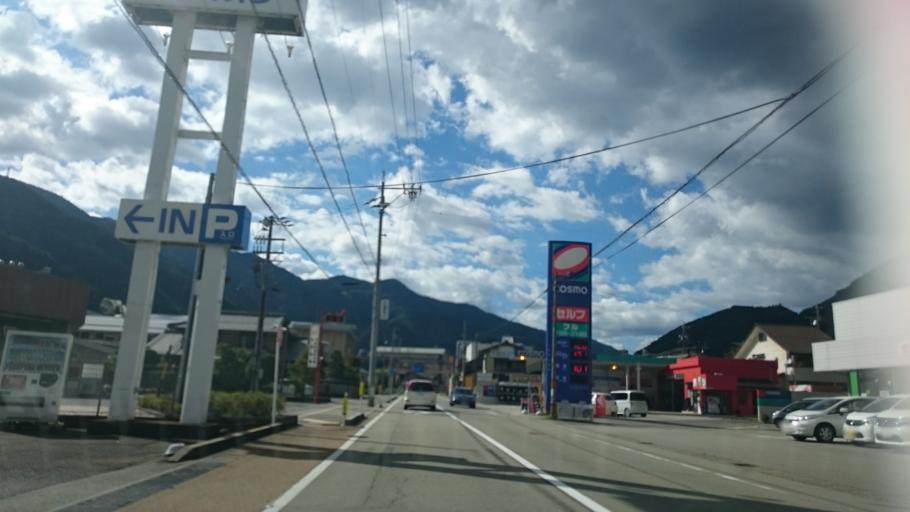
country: JP
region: Gifu
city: Gujo
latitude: 35.8007
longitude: 137.2494
